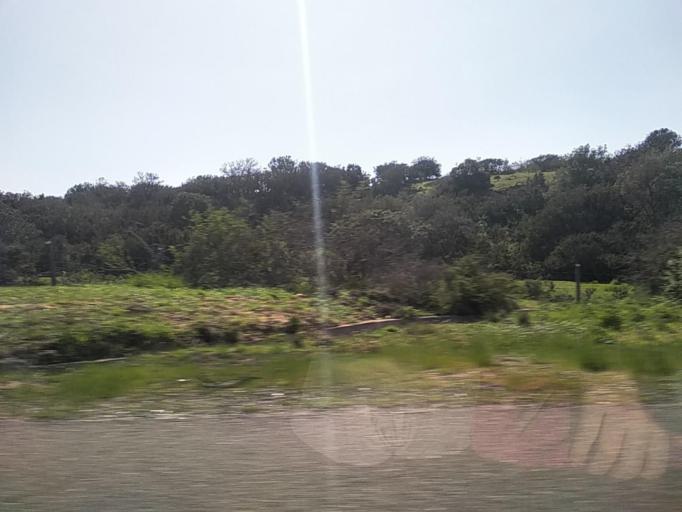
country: CL
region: Valparaiso
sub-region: San Antonio Province
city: El Tabo
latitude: -33.4059
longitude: -71.5299
